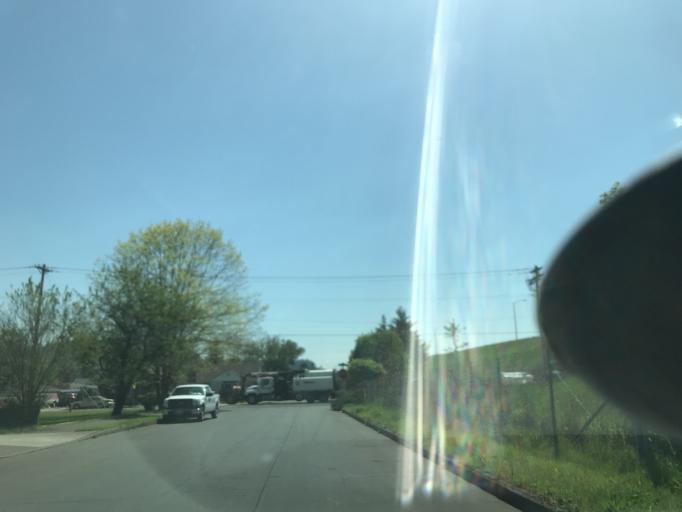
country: US
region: Oregon
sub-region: Multnomah County
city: Lents
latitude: 45.4834
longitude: -122.5648
